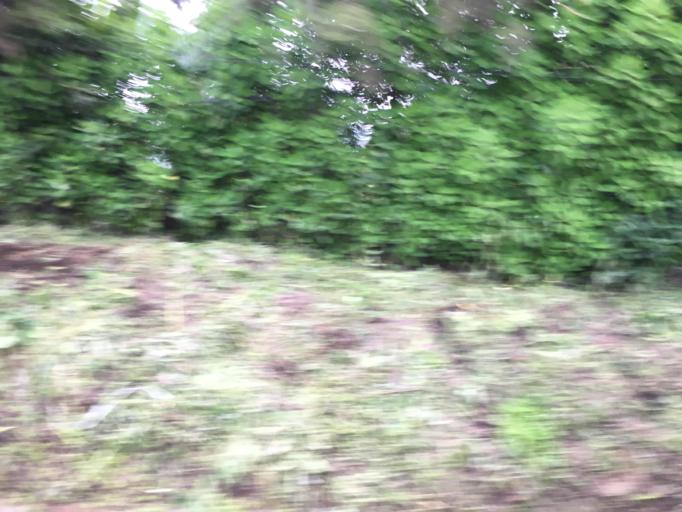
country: GT
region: Sacatepequez
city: San Miguel Duenas
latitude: 14.5152
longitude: -90.7810
